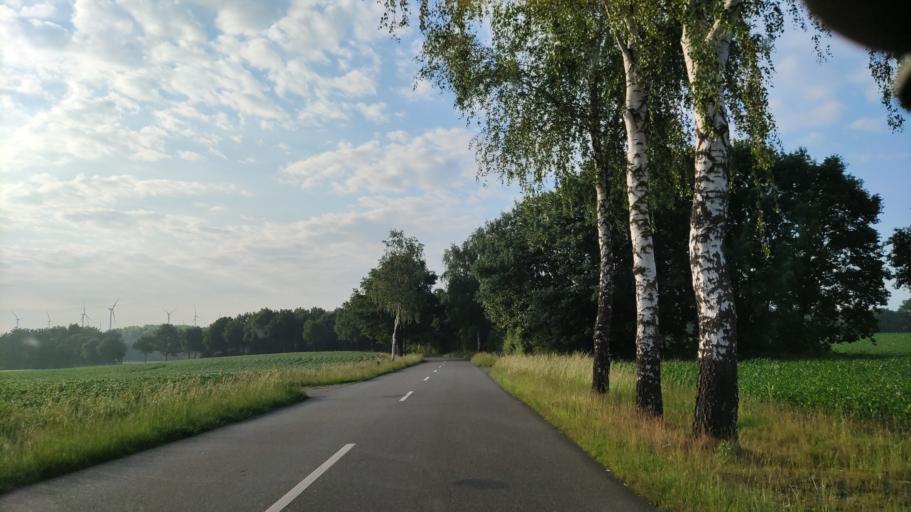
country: DE
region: Lower Saxony
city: Hanstedt Eins
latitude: 53.0299
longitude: 10.3548
